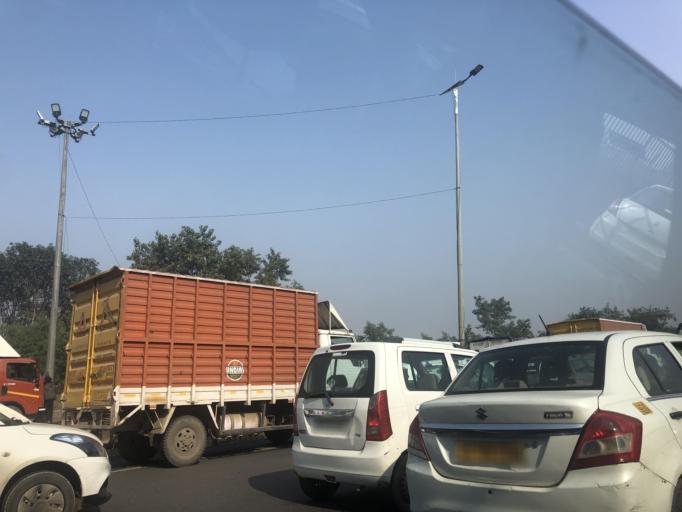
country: IN
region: Haryana
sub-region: Gurgaon
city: Gurgaon
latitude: 28.5345
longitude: 77.1095
